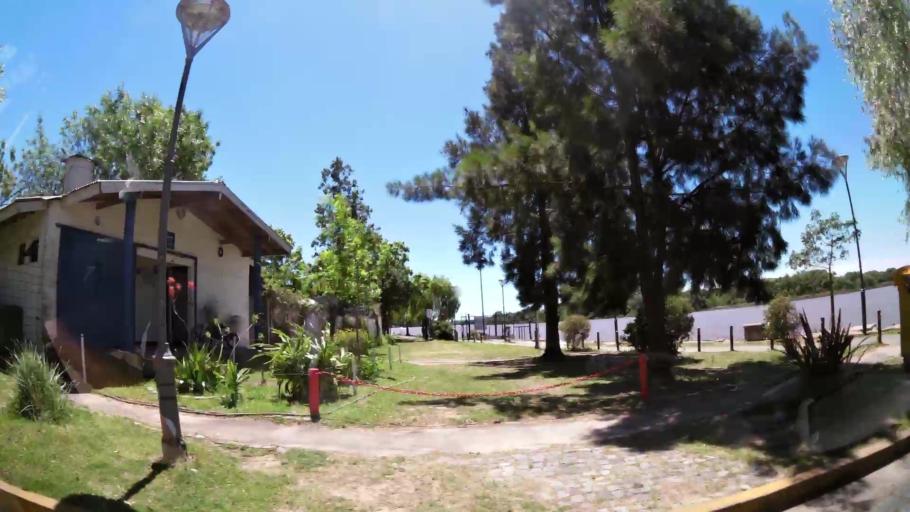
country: AR
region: Buenos Aires
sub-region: Partido de Tigre
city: Tigre
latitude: -34.4384
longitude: -58.5375
